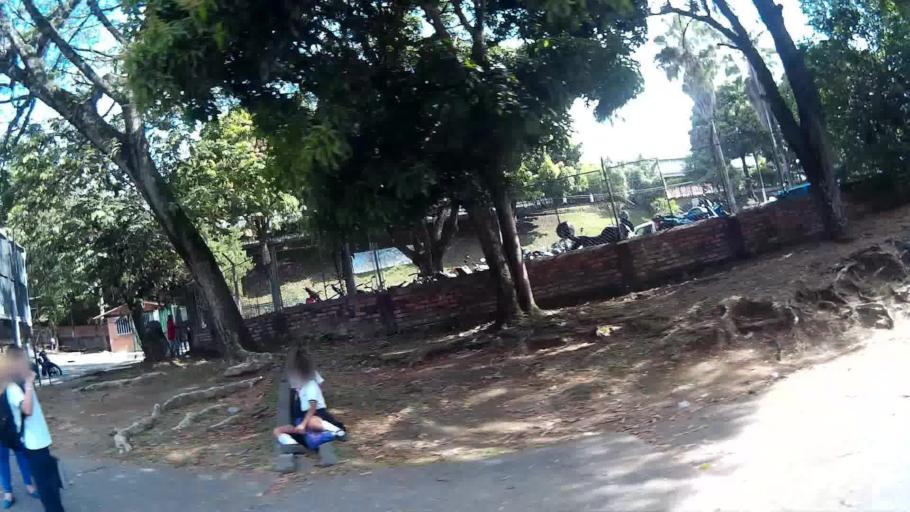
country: CO
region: Risaralda
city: Pereira
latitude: 4.8115
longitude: -75.7154
